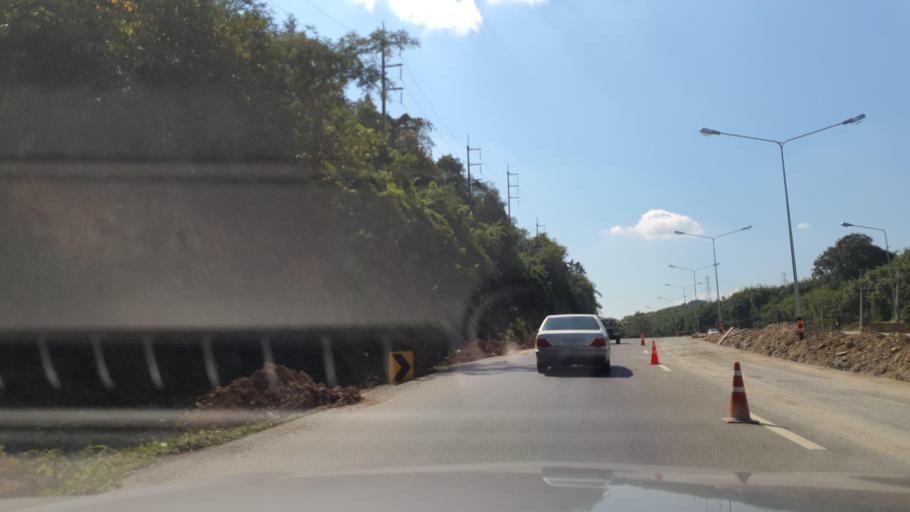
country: TH
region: Nan
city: Nan
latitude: 18.9181
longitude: 100.7656
